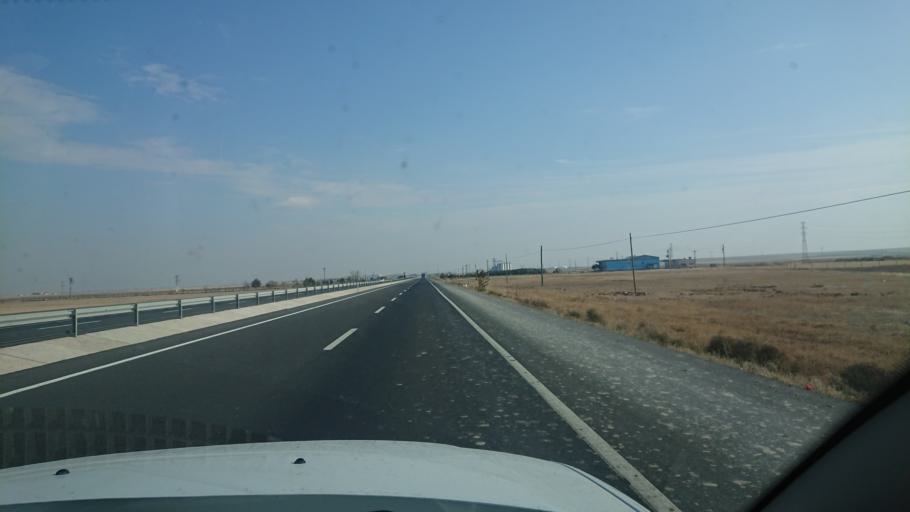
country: TR
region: Aksaray
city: Yesilova
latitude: 38.3170
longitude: 33.8545
